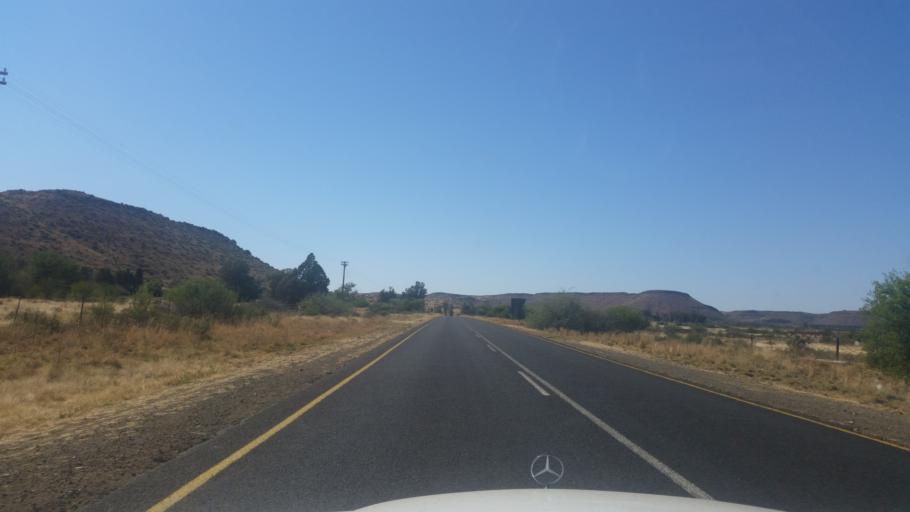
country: ZA
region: Orange Free State
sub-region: Xhariep District Municipality
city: Trompsburg
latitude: -30.4942
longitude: 25.9974
